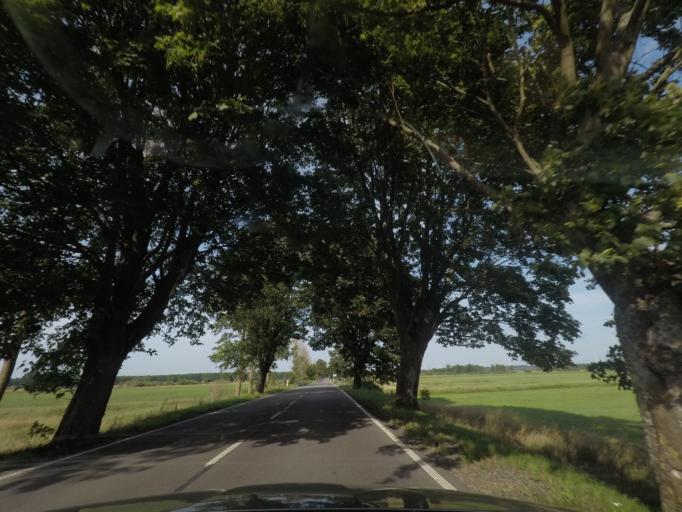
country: PL
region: Pomeranian Voivodeship
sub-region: Powiat leborski
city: Leba
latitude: 54.6508
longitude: 17.5567
